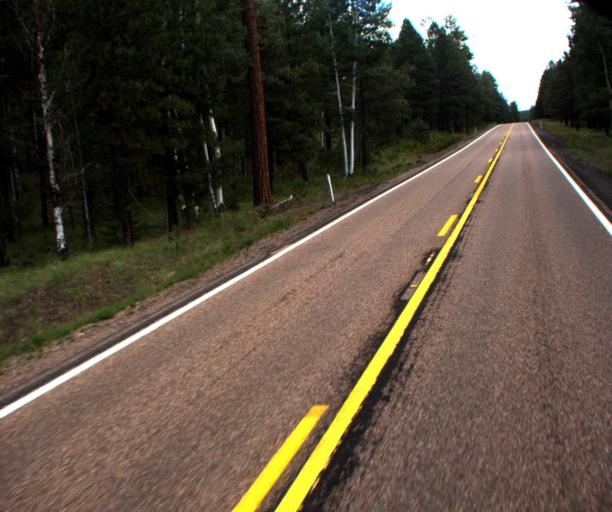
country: US
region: Arizona
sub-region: Navajo County
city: Pinetop-Lakeside
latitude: 34.0391
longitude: -109.6709
